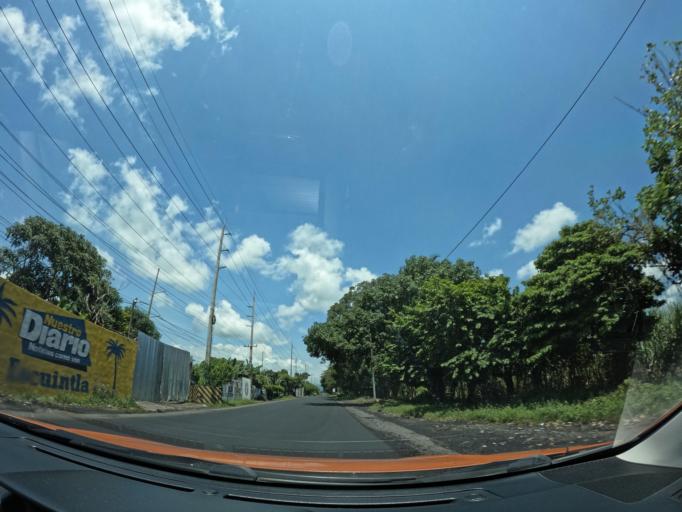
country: GT
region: Escuintla
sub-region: Municipio de Masagua
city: Masagua
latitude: 14.2154
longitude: -90.8353
